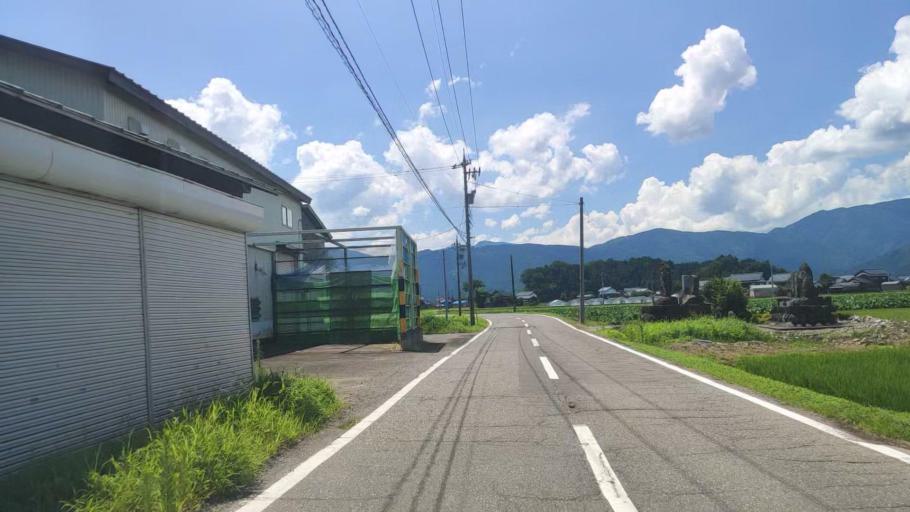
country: JP
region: Fukui
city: Ono
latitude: 35.9734
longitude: 136.5238
